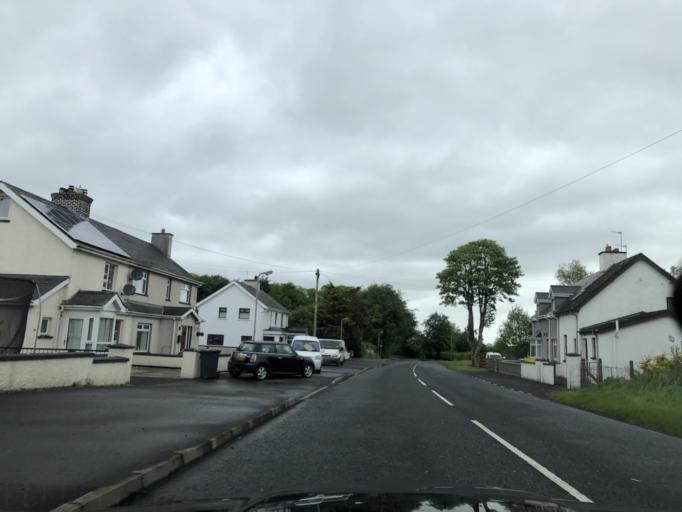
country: GB
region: Northern Ireland
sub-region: Ballymoney District
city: Ballymoney
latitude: 55.0872
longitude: -6.5086
